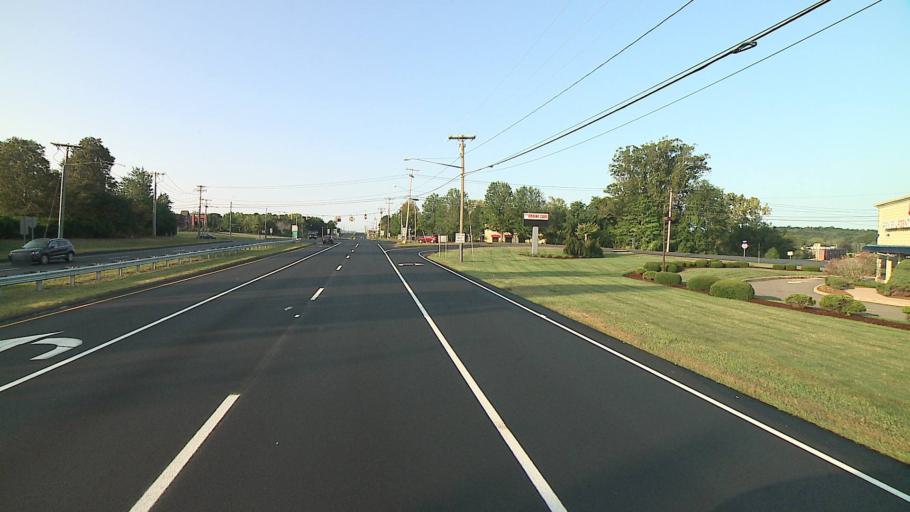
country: US
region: Connecticut
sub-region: Hartford County
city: Newington
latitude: 41.6707
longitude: -72.7175
